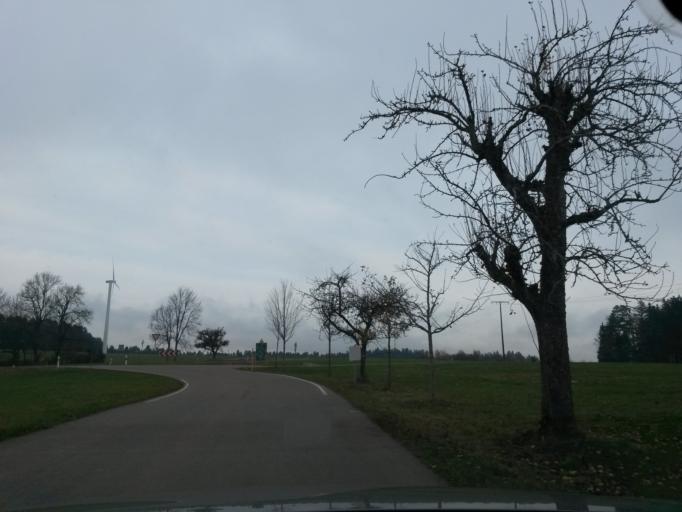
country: DE
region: Baden-Wuerttemberg
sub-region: Karlsruhe Region
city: Lossburg
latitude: 48.3897
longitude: 8.4509
